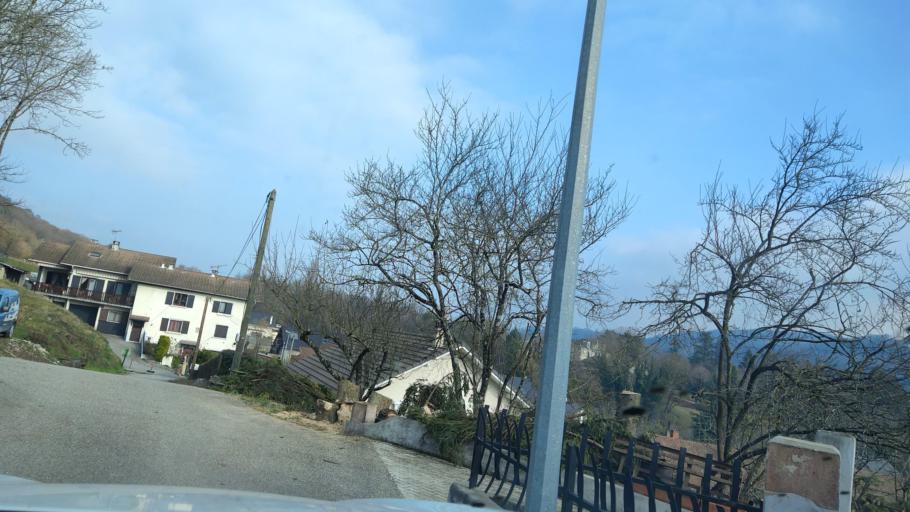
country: FR
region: Rhone-Alpes
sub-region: Departement de la Savoie
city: Gresy-sur-Aix
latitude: 45.7258
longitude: 5.9167
